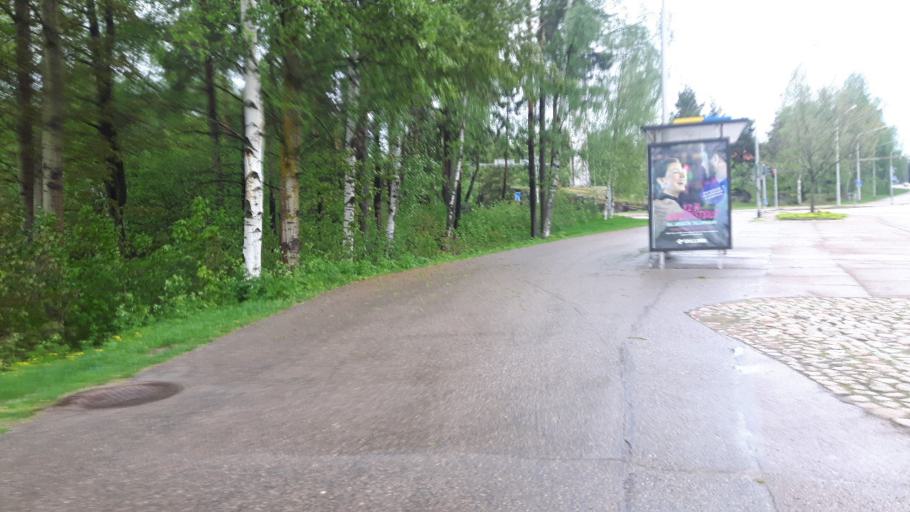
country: FI
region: Kymenlaakso
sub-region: Kotka-Hamina
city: Kotka
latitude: 60.4868
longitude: 26.9049
